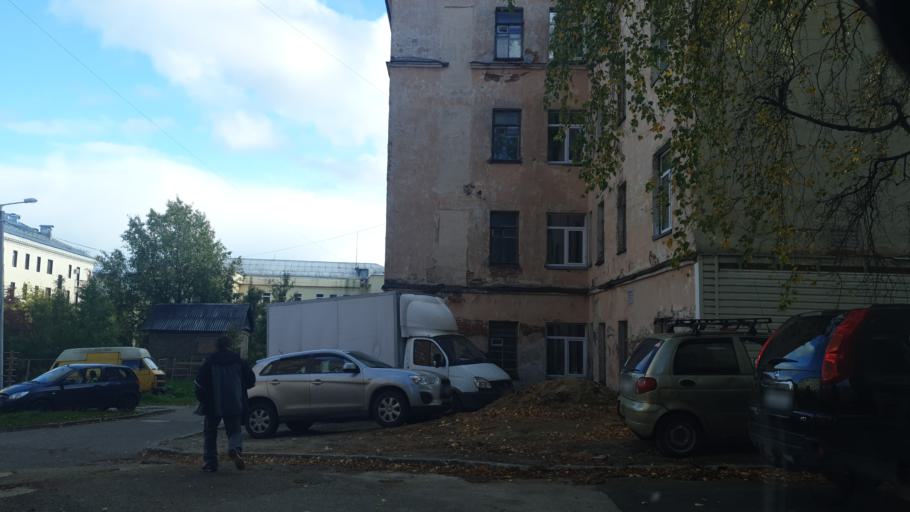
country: RU
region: Komi Republic
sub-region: Syktyvdinskiy Rayon
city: Syktyvkar
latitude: 61.6690
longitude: 50.8408
